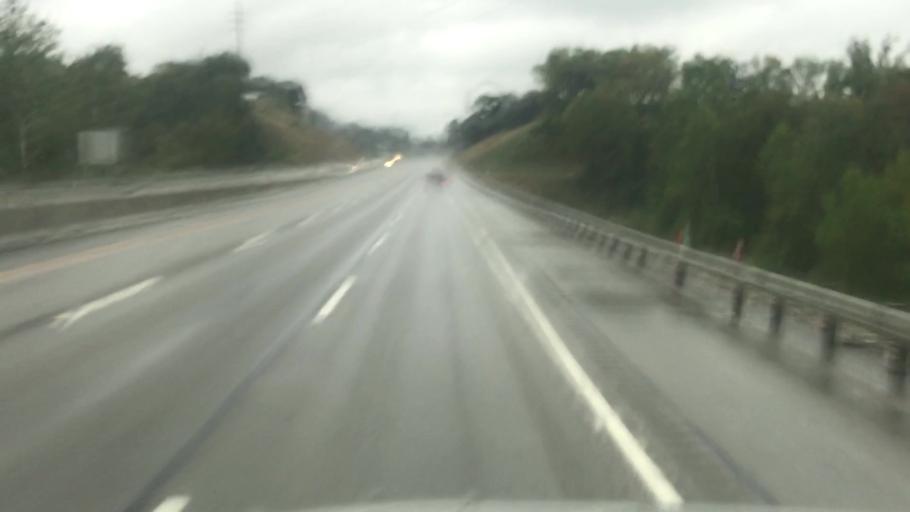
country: US
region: Pennsylvania
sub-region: Allegheny County
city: Oakmont
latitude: 40.5519
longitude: -79.8304
